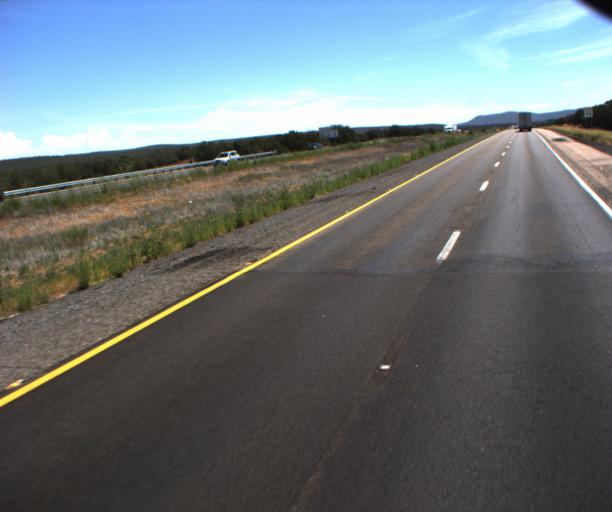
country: US
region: Arizona
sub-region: Mohave County
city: Peach Springs
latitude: 35.1908
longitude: -113.3530
